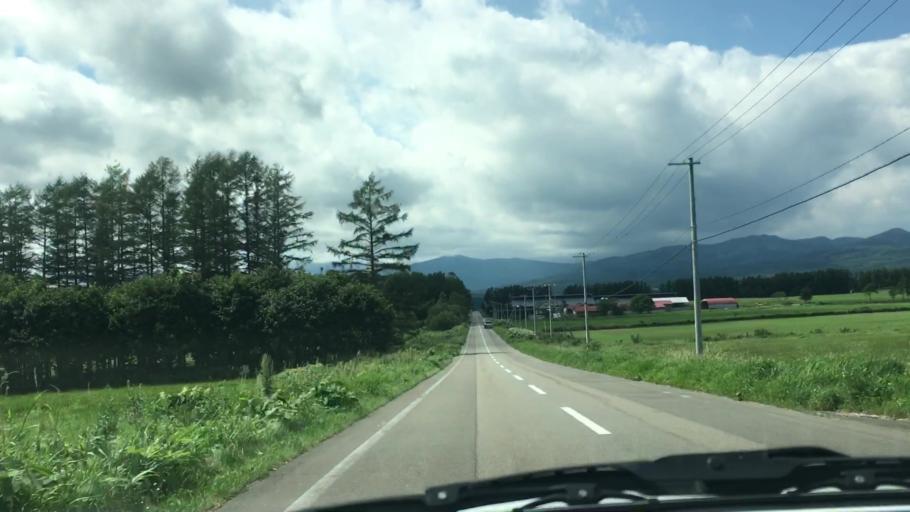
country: JP
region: Hokkaido
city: Otofuke
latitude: 43.2804
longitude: 143.3385
